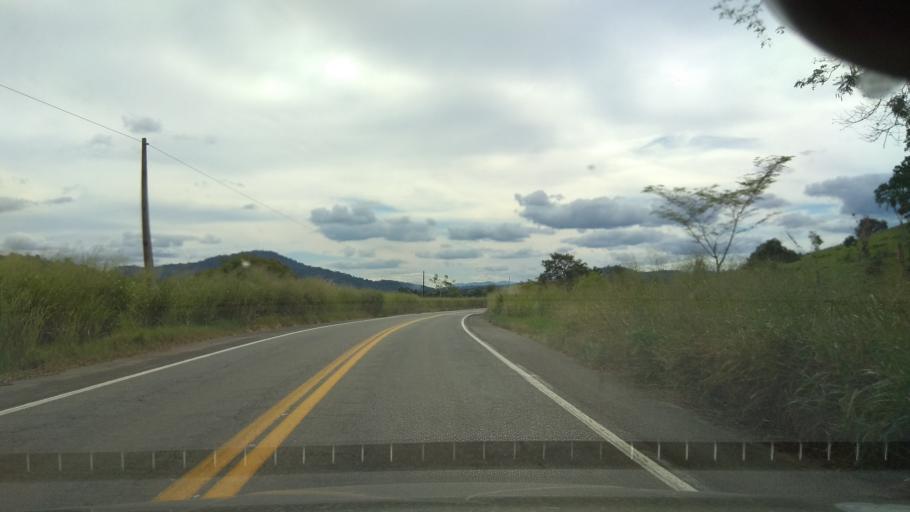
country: BR
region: Bahia
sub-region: Ipiau
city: Ipiau
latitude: -14.1889
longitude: -39.6582
